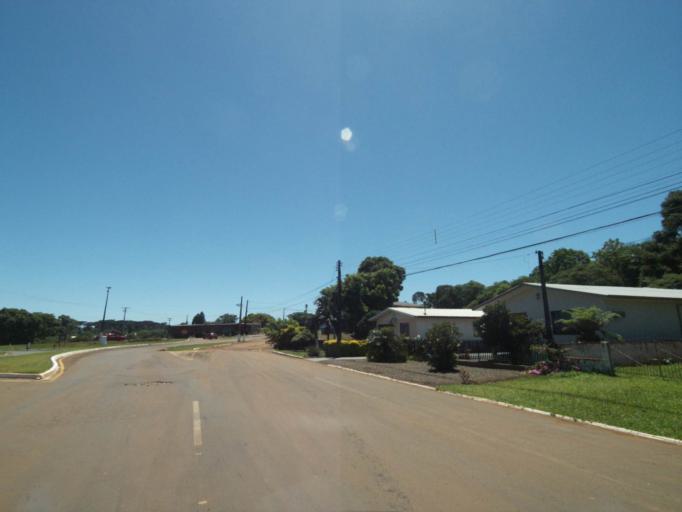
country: BR
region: Parana
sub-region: Pato Branco
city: Pato Branco
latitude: -26.2593
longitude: -52.7741
